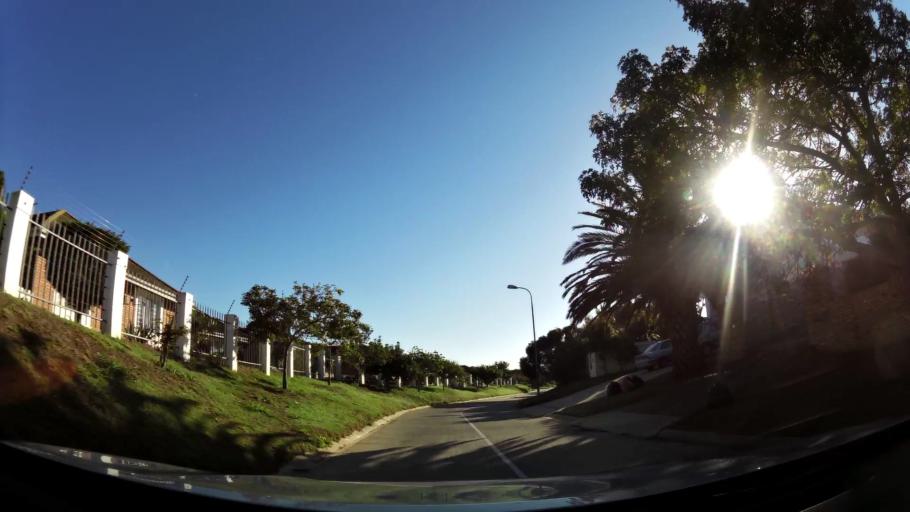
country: ZA
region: Eastern Cape
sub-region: Nelson Mandela Bay Metropolitan Municipality
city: Port Elizabeth
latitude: -33.9950
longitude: 25.6459
